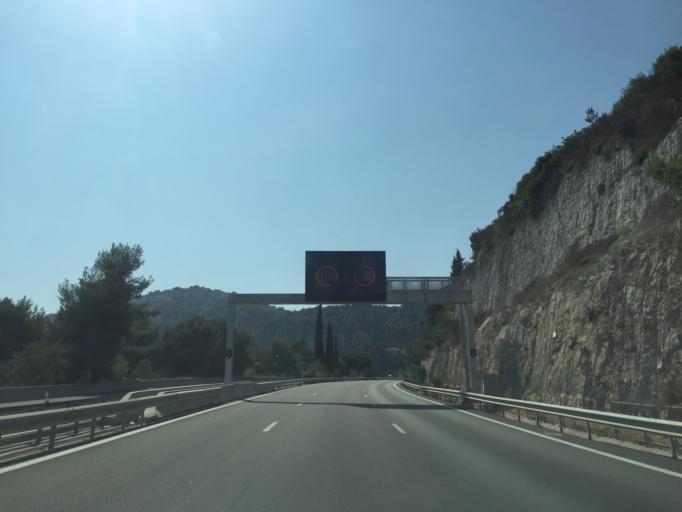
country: FR
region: Provence-Alpes-Cote d'Azur
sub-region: Departement des Alpes-Maritimes
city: Beausoleil
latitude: 43.7516
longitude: 7.4090
